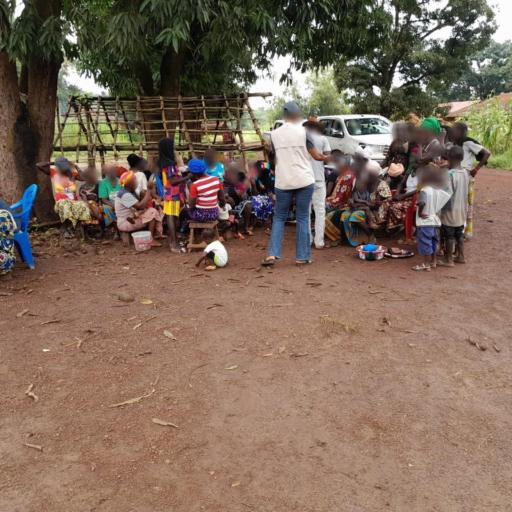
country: GN
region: Boke
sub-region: Boke Prefecture
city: Boke
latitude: 11.0606
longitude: -14.4486
